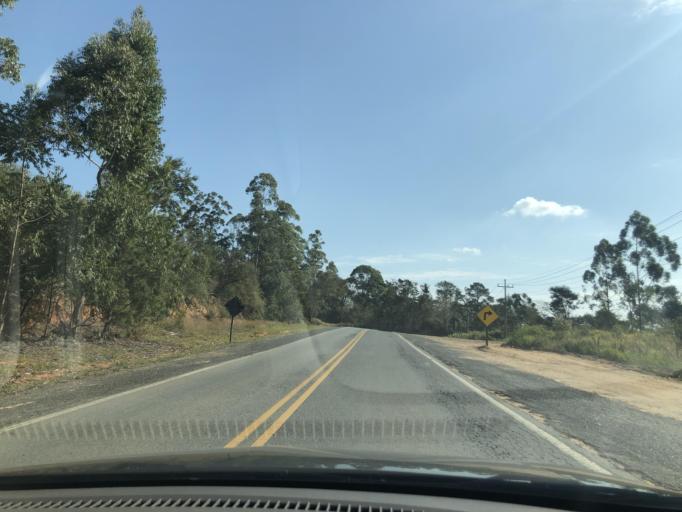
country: BR
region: Sao Paulo
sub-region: Pilar Do Sul
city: Pilar do Sul
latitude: -23.8288
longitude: -47.6723
